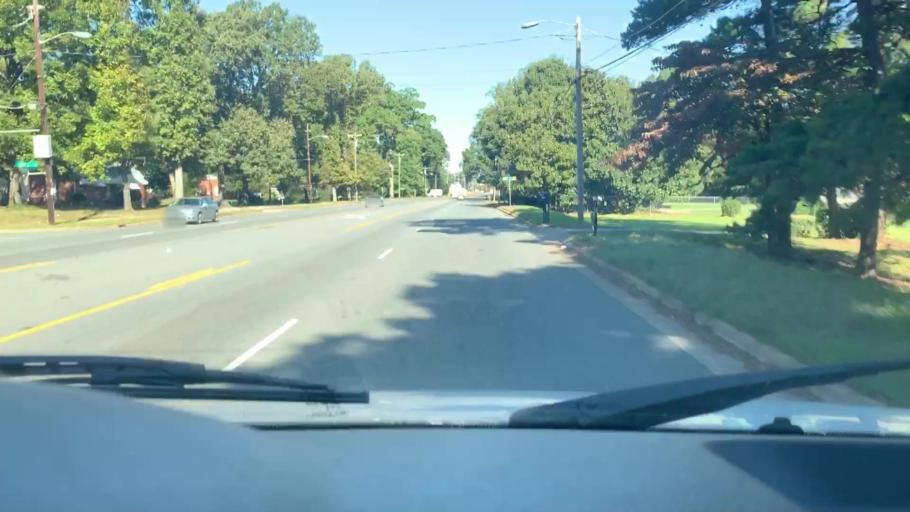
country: US
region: North Carolina
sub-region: Mecklenburg County
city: Charlotte
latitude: 35.2860
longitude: -80.7939
